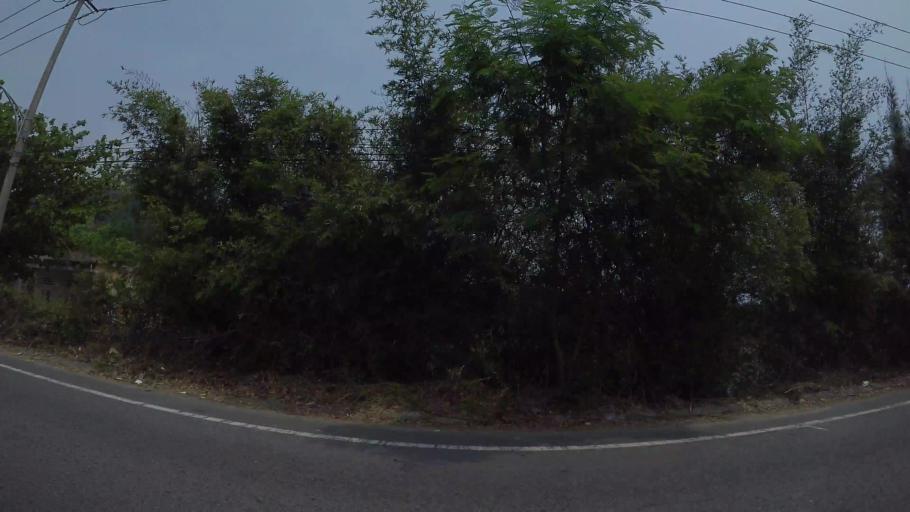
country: VN
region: Da Nang
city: Son Tra
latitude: 16.0992
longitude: 108.2664
